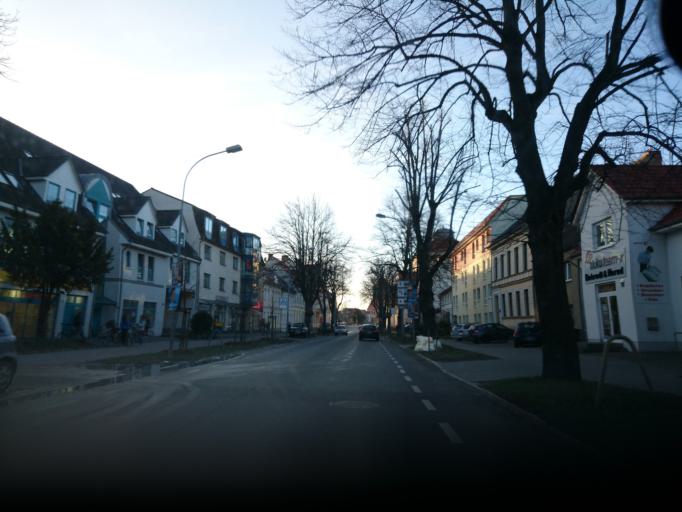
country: DE
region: Mecklenburg-Vorpommern
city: Greifswald
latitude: 54.0925
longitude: 13.3903
